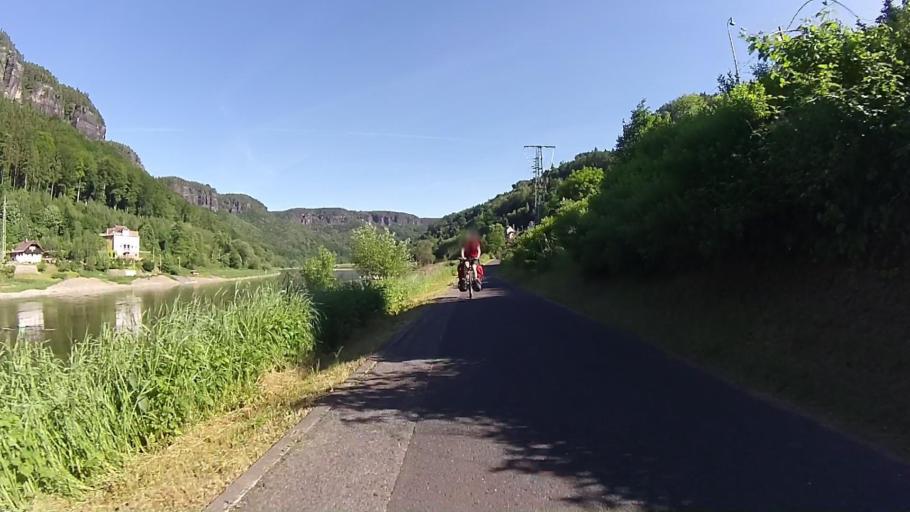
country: CZ
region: Ustecky
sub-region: Okres Decin
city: Decin
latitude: 50.8442
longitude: 14.2166
